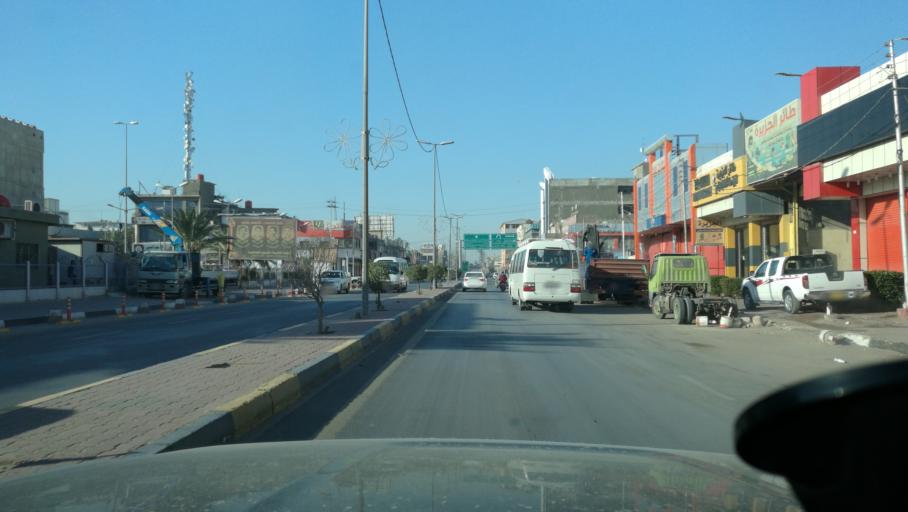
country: IQ
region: Basra Governorate
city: Al Basrah al Qadimah
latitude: 30.5057
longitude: 47.8342
